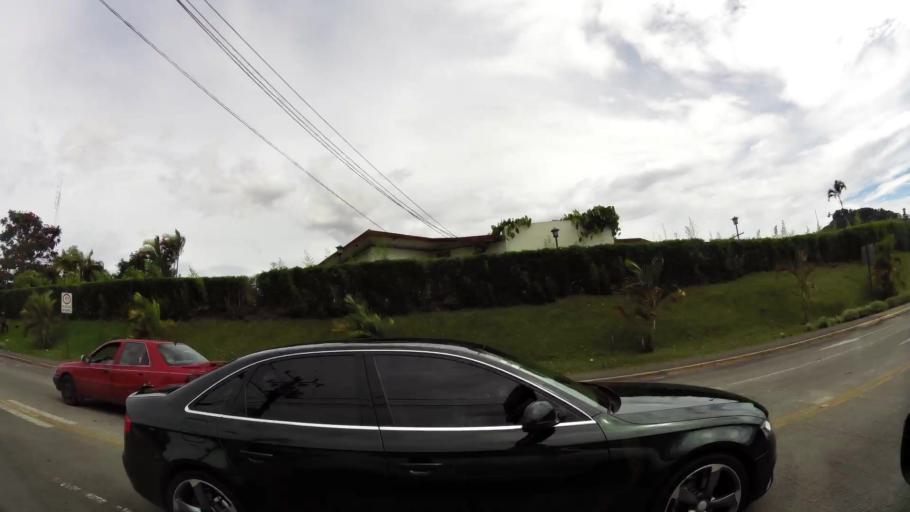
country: CR
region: San Jose
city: Curridabat
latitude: 9.9069
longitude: -84.0500
